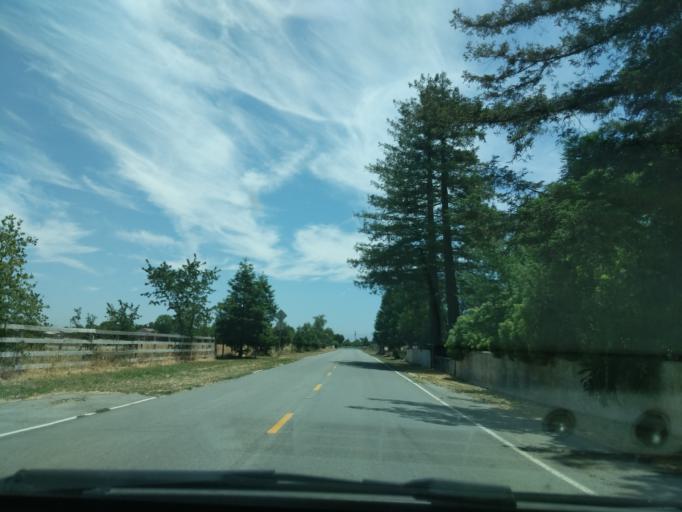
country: US
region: California
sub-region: Santa Clara County
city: Gilroy
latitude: 37.0522
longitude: -121.5581
